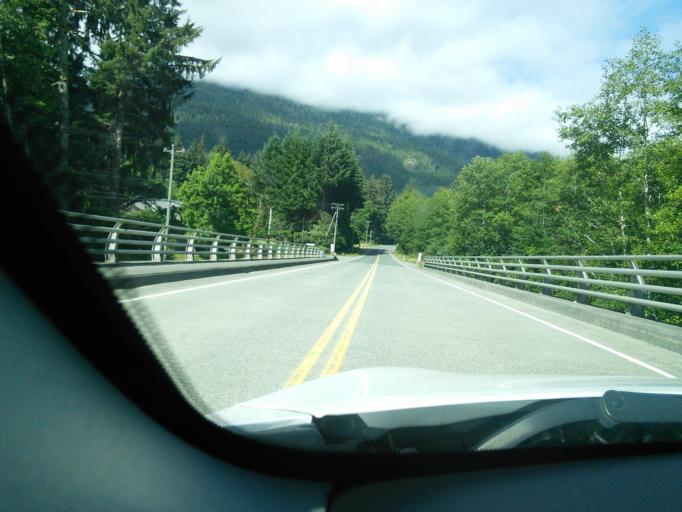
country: CA
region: British Columbia
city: Campbell River
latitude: 50.3615
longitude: -125.9209
